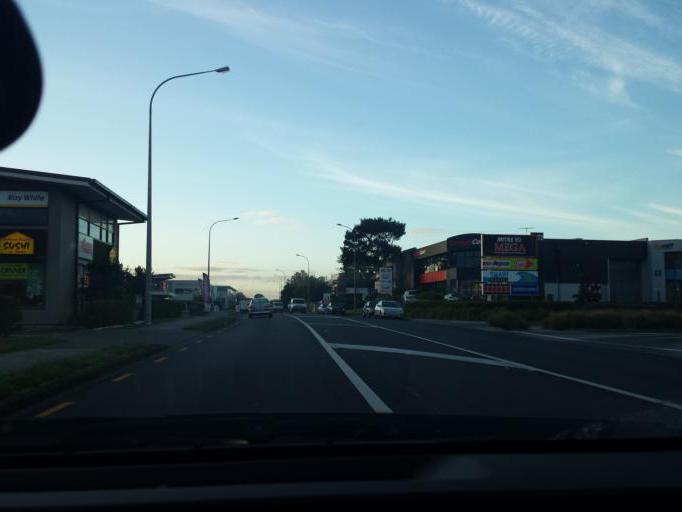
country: NZ
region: Auckland
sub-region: Auckland
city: Tamaki
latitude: -36.8908
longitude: 174.8346
